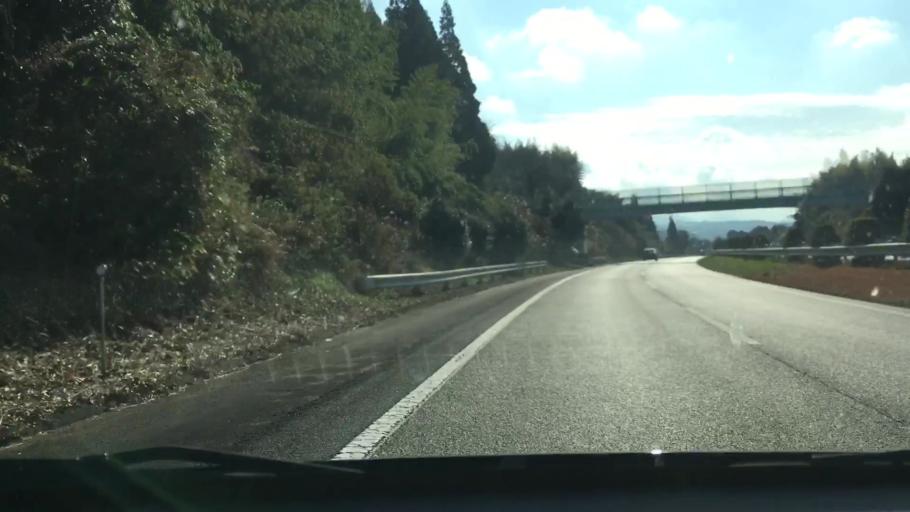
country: JP
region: Kumamoto
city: Matsubase
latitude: 32.6085
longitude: 130.7242
